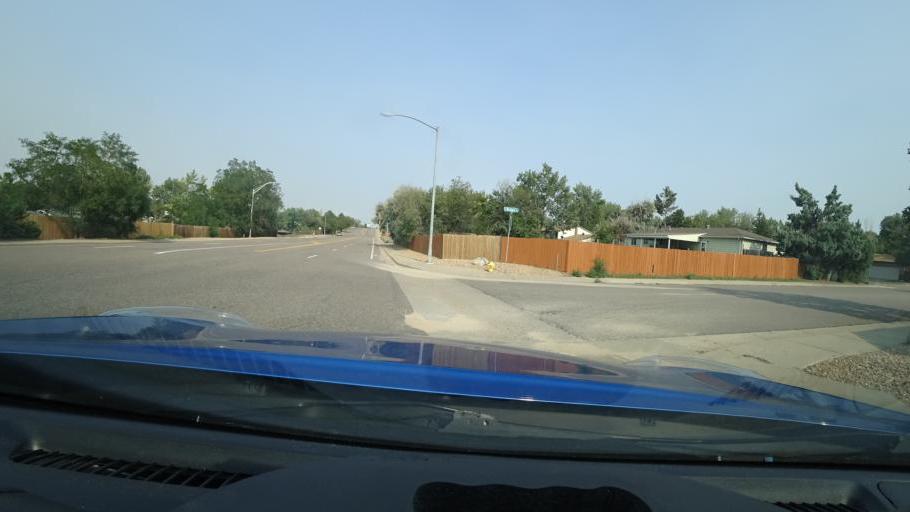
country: US
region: Colorado
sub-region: Adams County
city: Aurora
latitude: 39.6675
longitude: -104.7955
